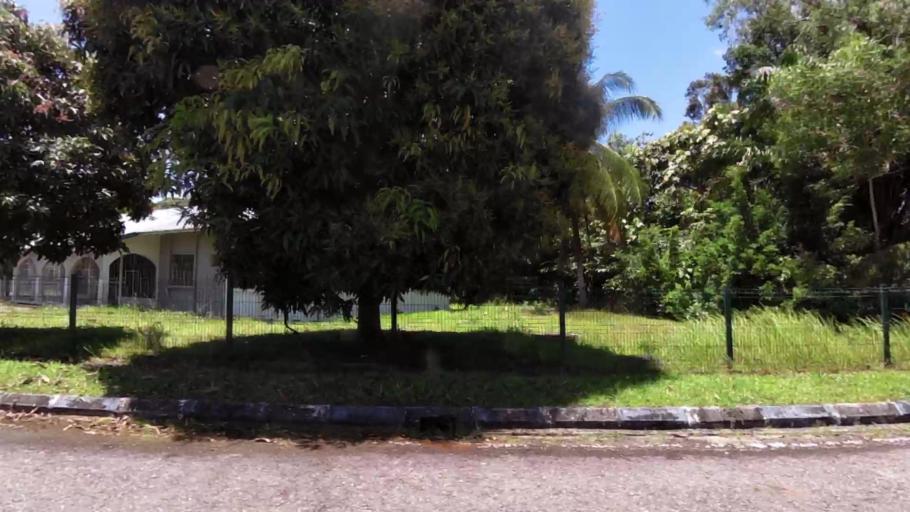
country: BN
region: Brunei and Muara
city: Bandar Seri Begawan
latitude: 4.9214
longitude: 114.9612
